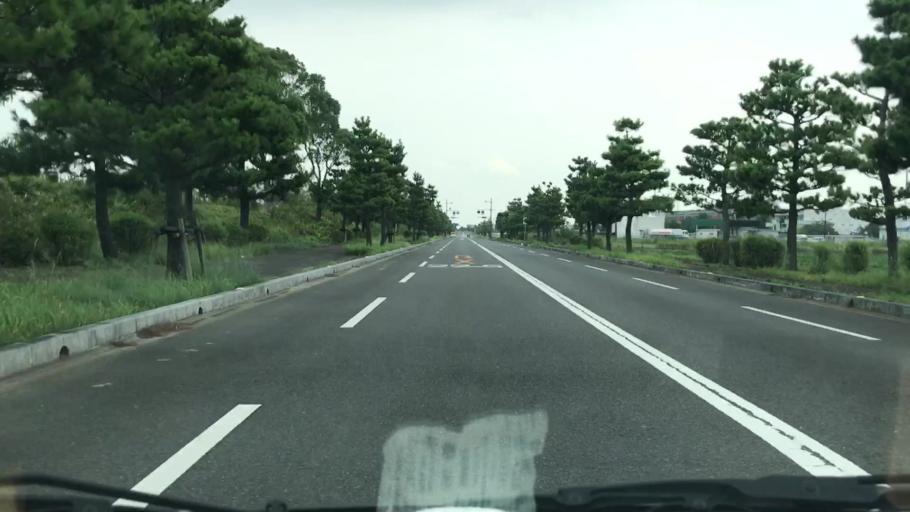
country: JP
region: Saga Prefecture
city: Okawa
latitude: 33.1561
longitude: 130.2997
